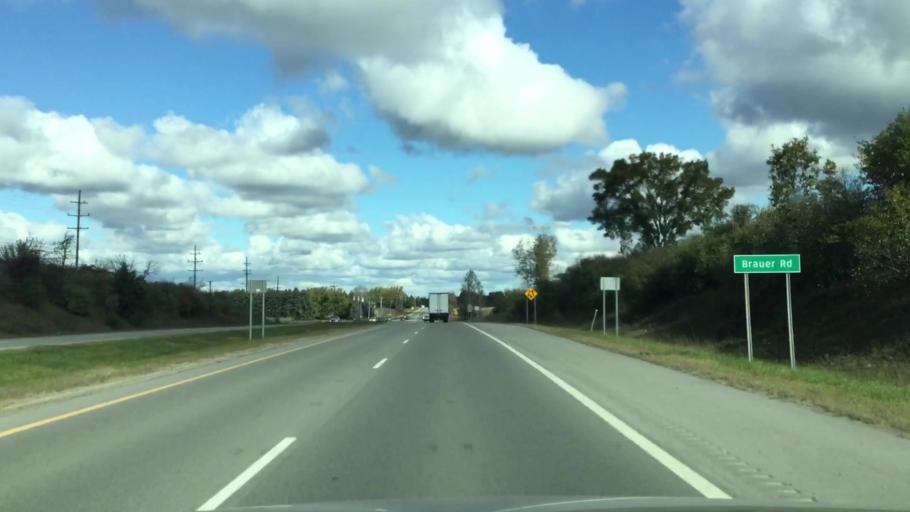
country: US
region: Michigan
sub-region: Oakland County
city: Oxford
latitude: 42.8957
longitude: -83.3114
